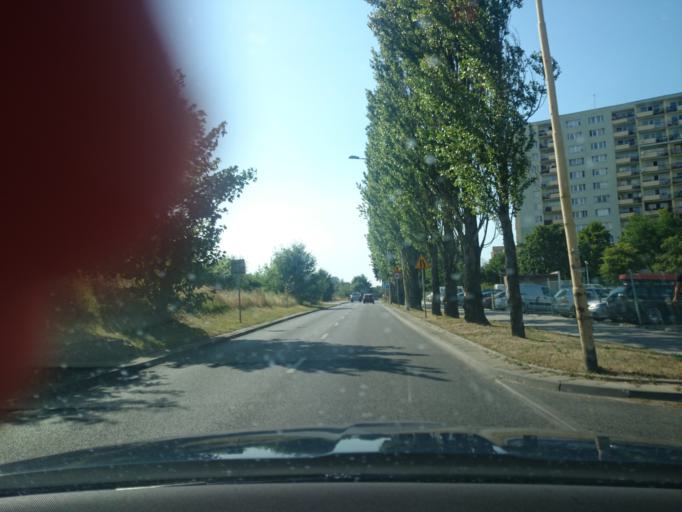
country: PL
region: West Pomeranian Voivodeship
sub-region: Szczecin
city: Szczecin
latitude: 53.3747
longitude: 14.6537
